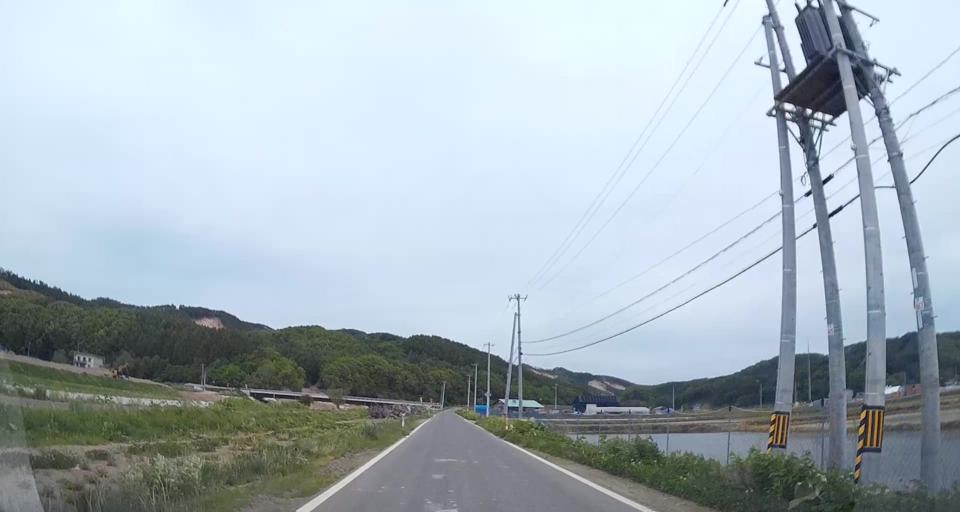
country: JP
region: Hokkaido
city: Chitose
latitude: 42.7543
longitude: 141.9714
